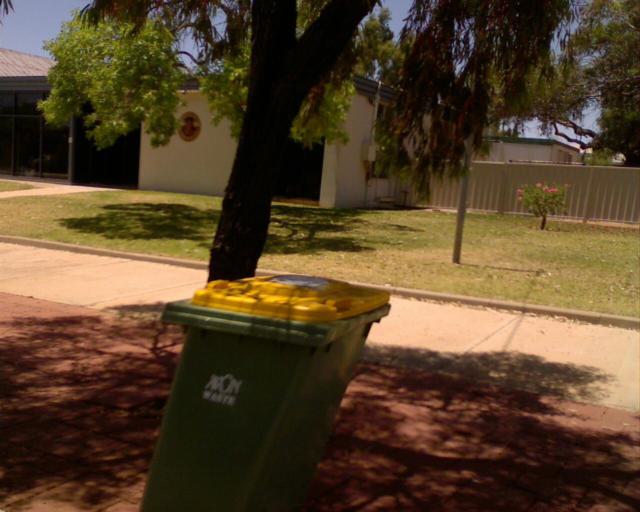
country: AU
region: Western Australia
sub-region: Merredin
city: Merredin
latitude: -30.8122
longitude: 117.8622
